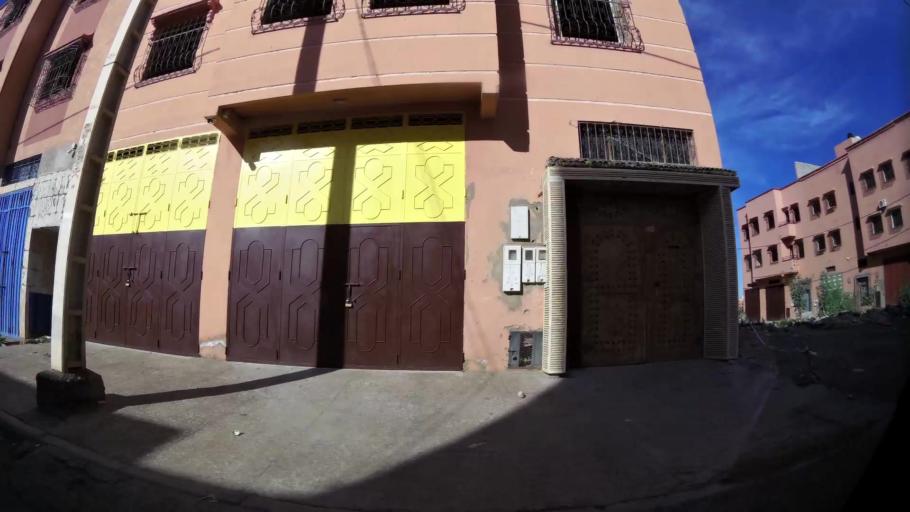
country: MA
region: Marrakech-Tensift-Al Haouz
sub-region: Marrakech
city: Marrakesh
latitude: 31.6790
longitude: -8.0419
